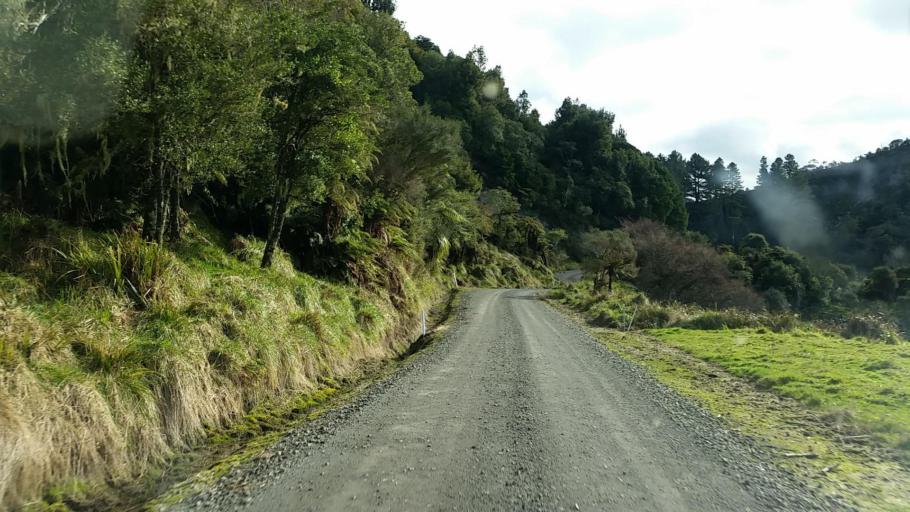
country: NZ
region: Taranaki
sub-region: New Plymouth District
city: Waitara
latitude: -39.0984
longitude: 174.5674
